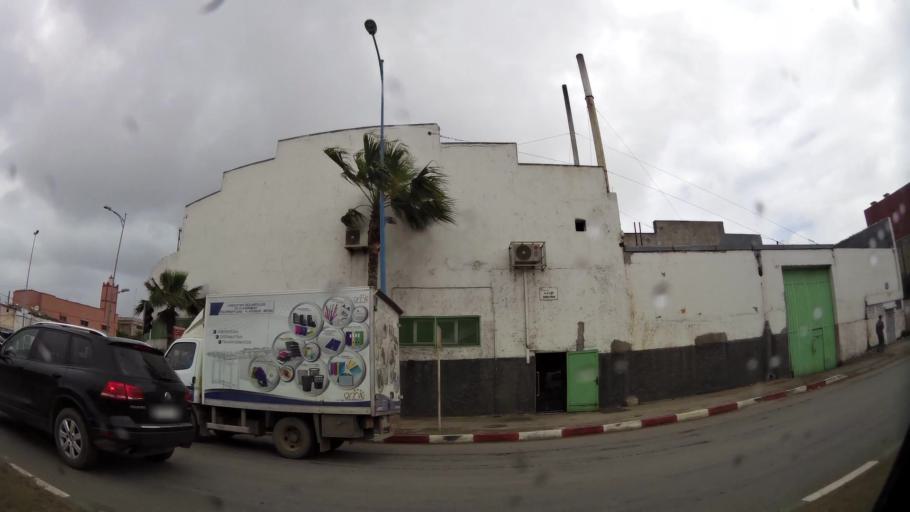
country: MA
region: Grand Casablanca
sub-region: Mediouna
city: Tit Mellil
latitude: 33.6236
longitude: -7.5062
